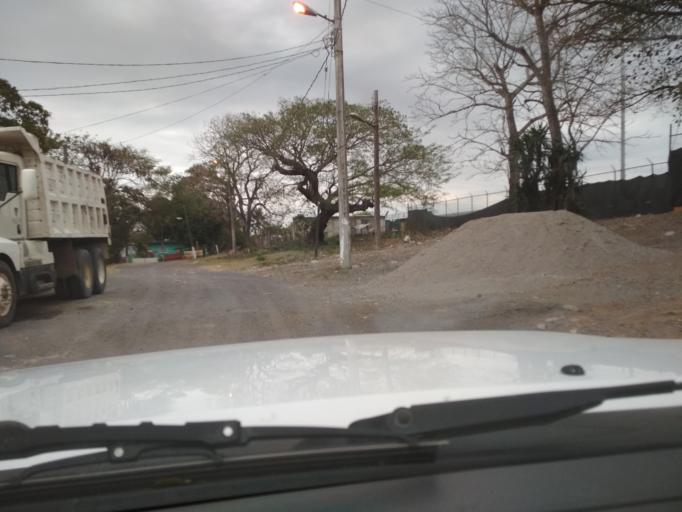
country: MX
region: Veracruz
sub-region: Veracruz
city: Delfino Victoria (Santa Fe)
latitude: 19.1689
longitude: -96.2618
